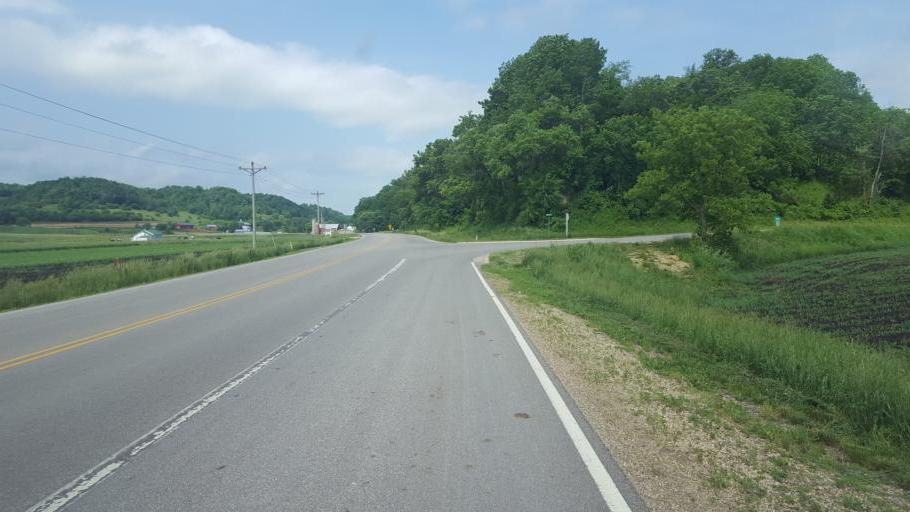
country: US
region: Wisconsin
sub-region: Monroe County
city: Cashton
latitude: 43.7327
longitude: -90.6750
